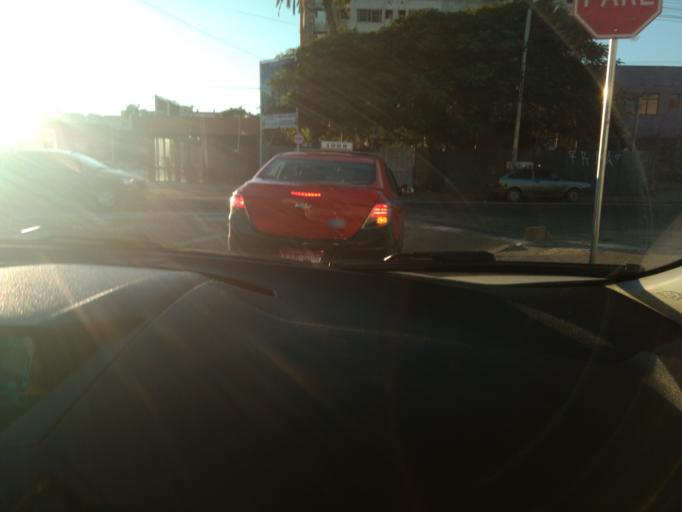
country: BR
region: Rio Grande do Sul
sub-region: Porto Alegre
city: Porto Alegre
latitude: -30.0667
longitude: -51.2129
